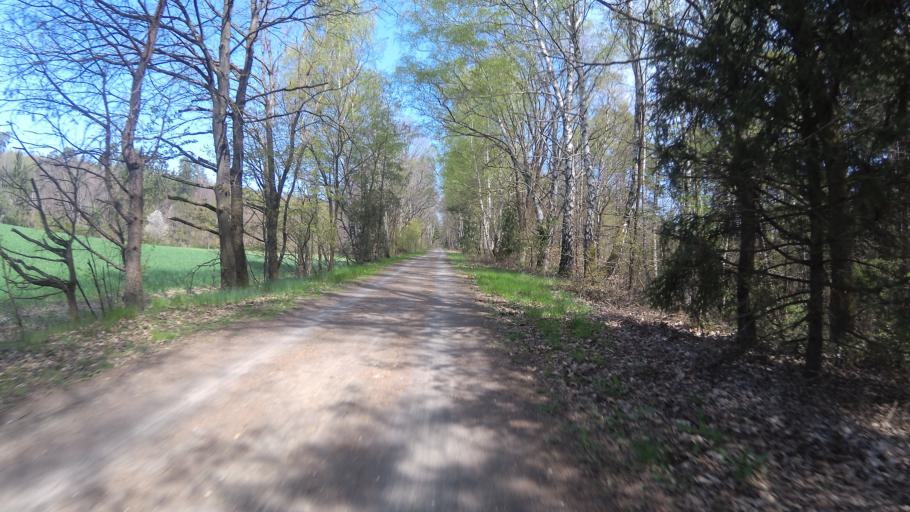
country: DE
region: Rheinland-Pfalz
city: Schonenberg-Kubelberg
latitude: 49.3927
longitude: 7.3557
